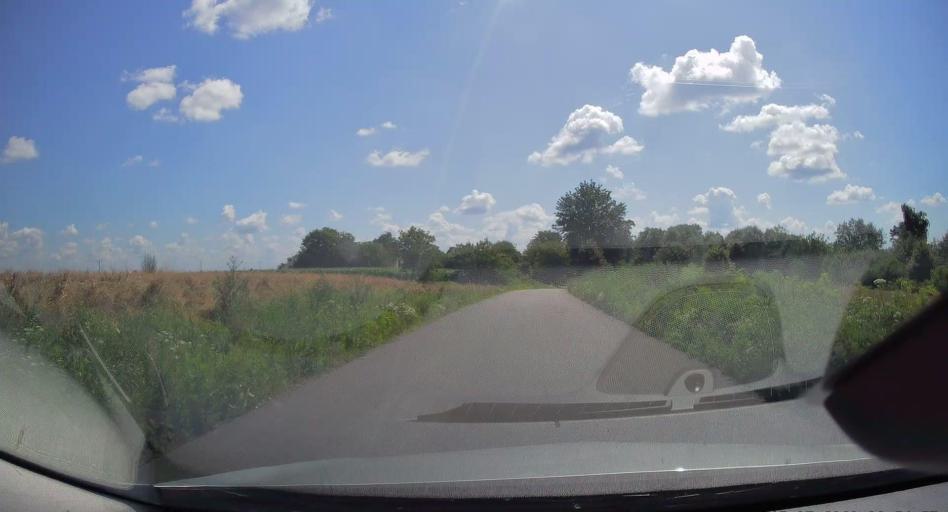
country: PL
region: Subcarpathian Voivodeship
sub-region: Powiat jaroslawski
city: Sosnica
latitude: 49.8663
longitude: 22.8682
